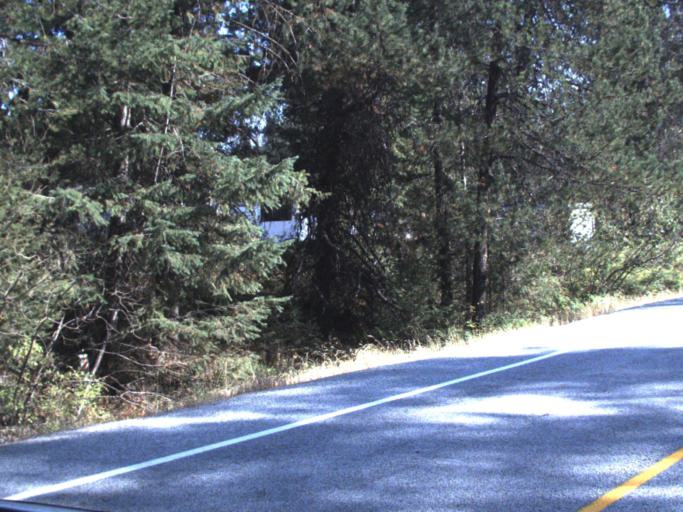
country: US
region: Washington
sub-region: Pend Oreille County
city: Newport
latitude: 48.1249
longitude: -117.2743
